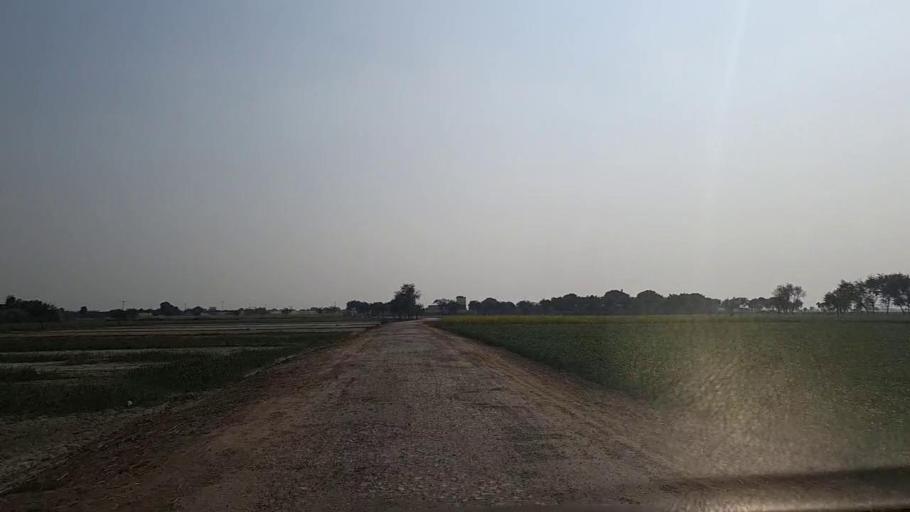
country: PK
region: Sindh
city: Daur
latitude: 26.4026
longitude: 68.4176
